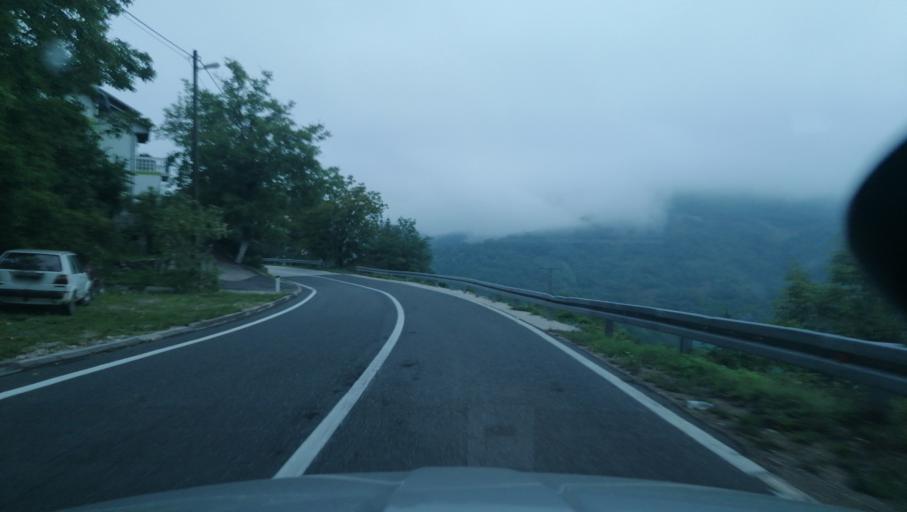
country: BA
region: Federation of Bosnia and Herzegovina
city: Jablanica
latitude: 43.7098
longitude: 17.7172
